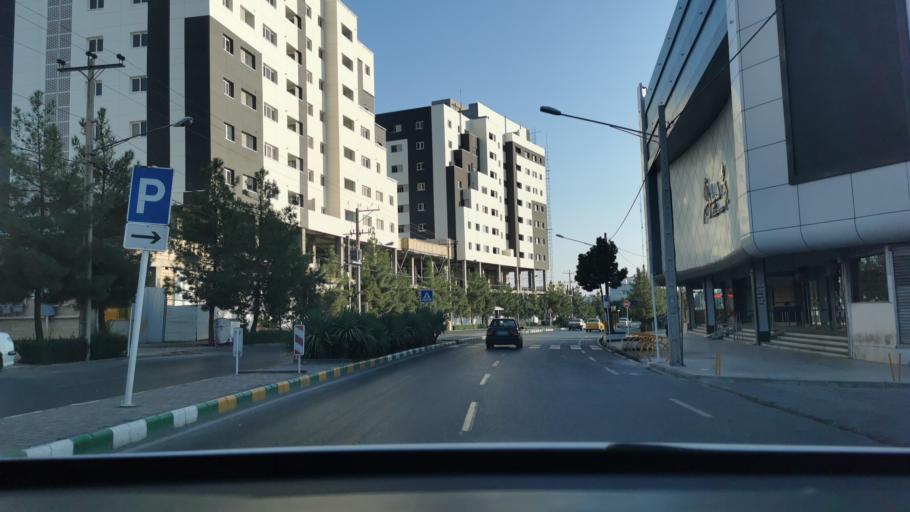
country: IR
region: Razavi Khorasan
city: Mashhad
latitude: 36.3602
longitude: 59.5131
